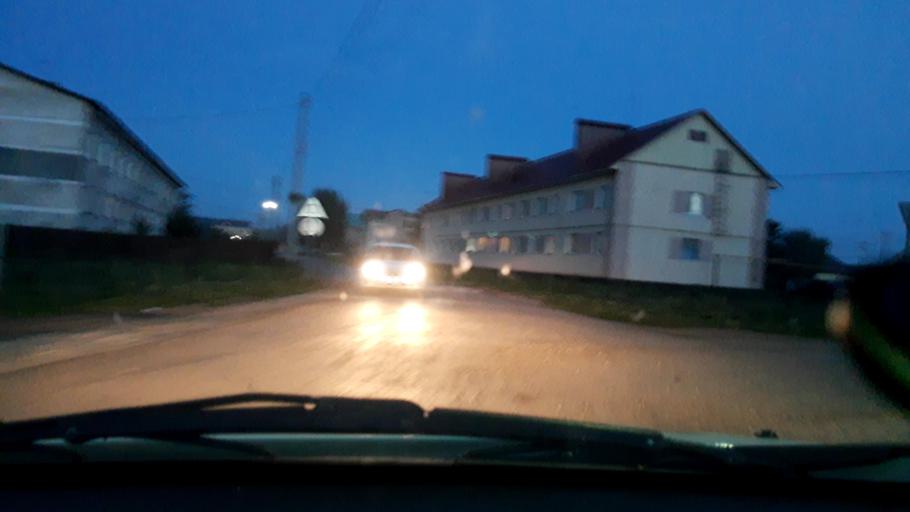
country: RU
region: Bashkortostan
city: Ulukulevo
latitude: 54.4236
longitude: 56.3361
